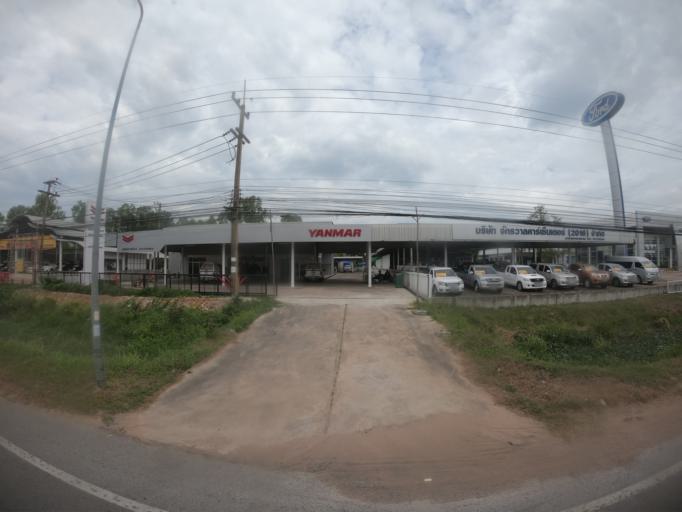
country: TH
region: Maha Sarakham
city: Maha Sarakham
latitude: 16.1660
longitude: 103.3312
